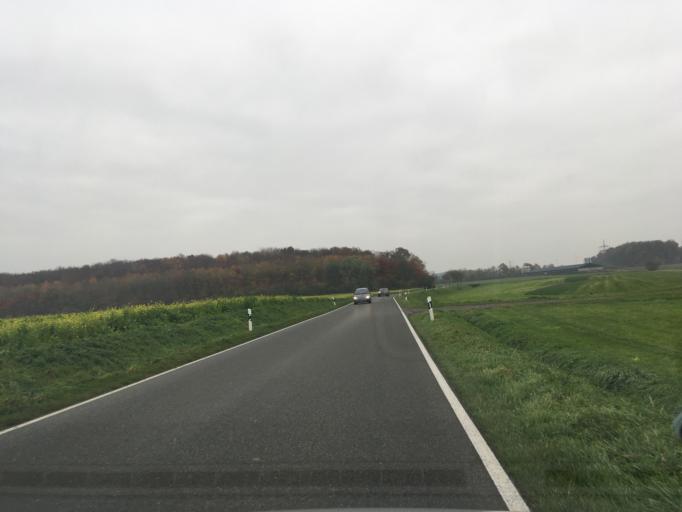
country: DE
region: North Rhine-Westphalia
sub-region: Regierungsbezirk Munster
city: Legden
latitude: 52.0337
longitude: 7.1373
